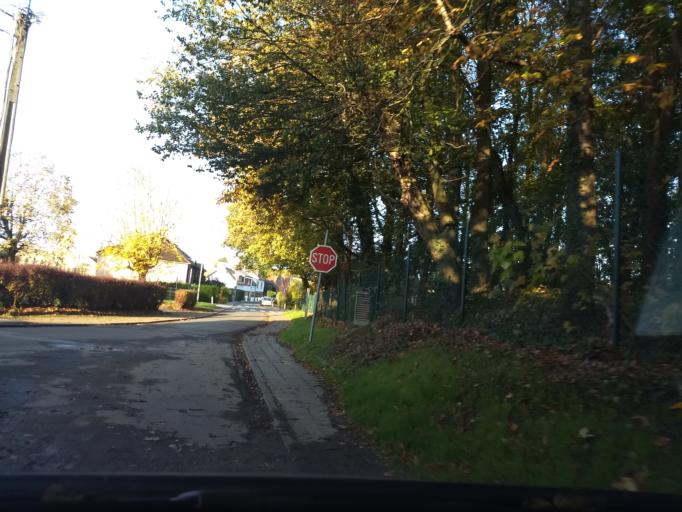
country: BE
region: Wallonia
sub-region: Province du Brabant Wallon
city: Braine-l'Alleud
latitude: 50.6754
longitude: 4.3775
